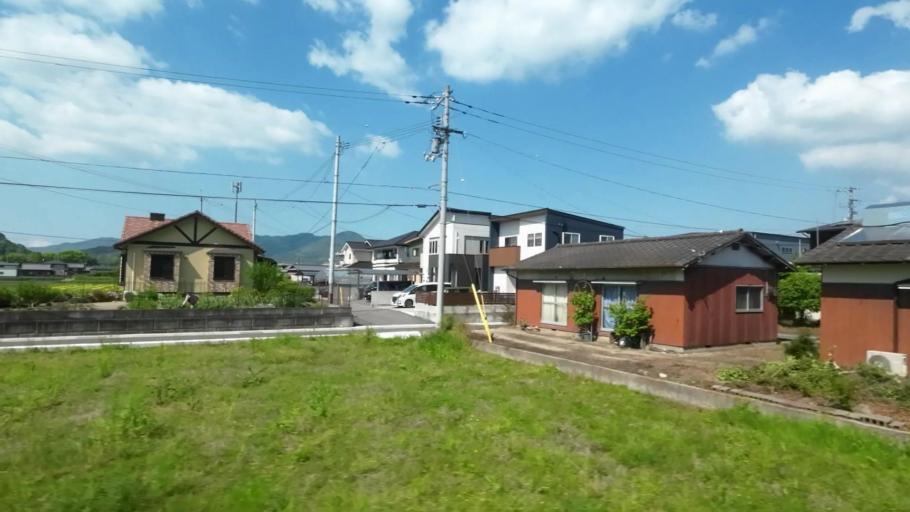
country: JP
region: Kagawa
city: Tadotsu
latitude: 34.2046
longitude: 133.7110
